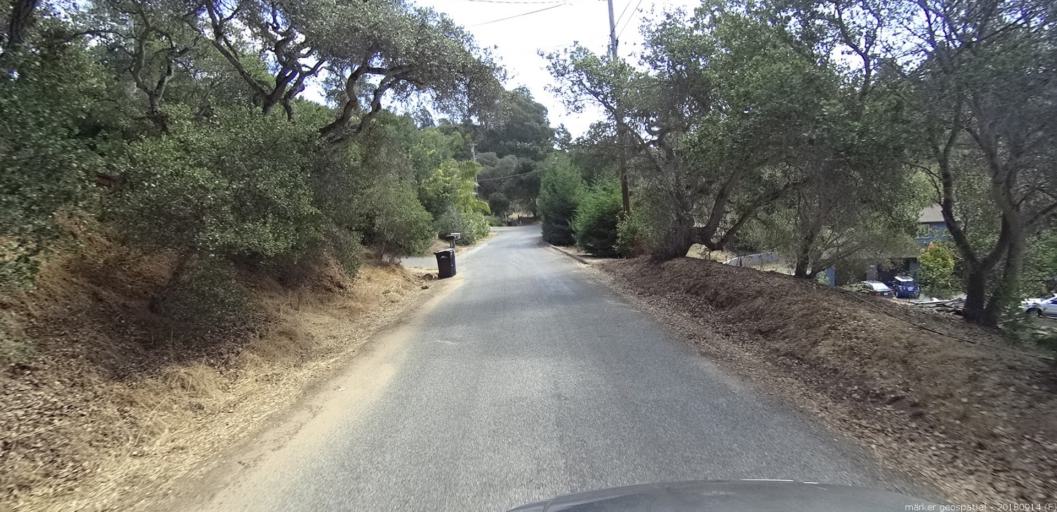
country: US
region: California
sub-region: San Benito County
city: Aromas
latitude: 36.8686
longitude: -121.6499
